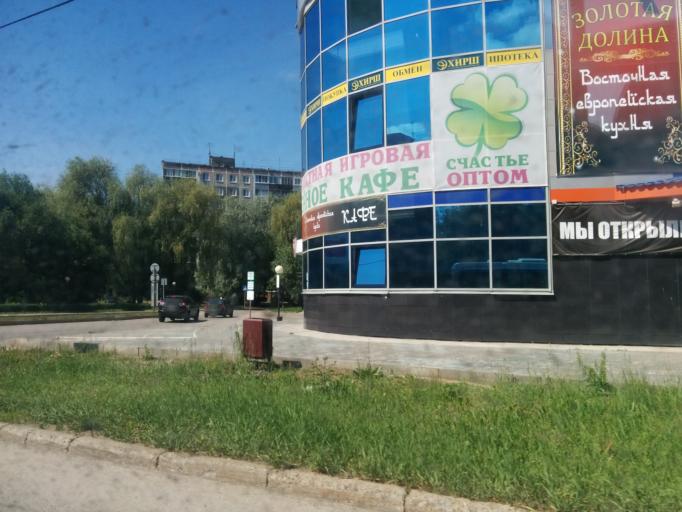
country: RU
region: Perm
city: Perm
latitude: 58.0003
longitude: 56.2969
